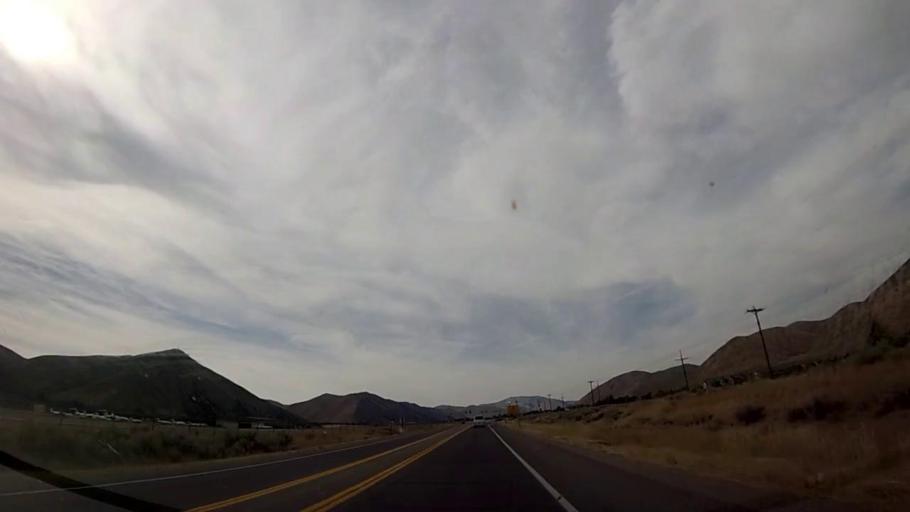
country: US
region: Idaho
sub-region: Blaine County
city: Hailey
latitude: 43.4968
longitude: -114.2870
